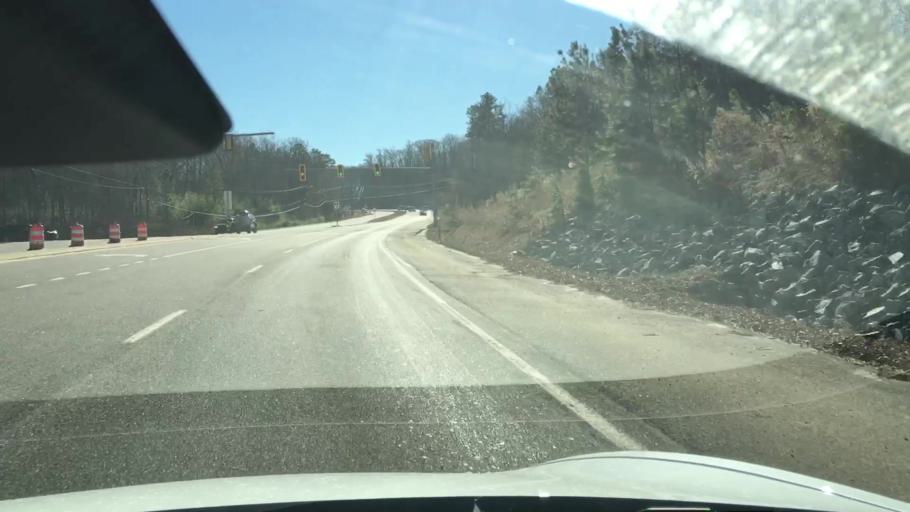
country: US
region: Virginia
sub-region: Chesterfield County
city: Bon Air
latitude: 37.5479
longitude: -77.6536
